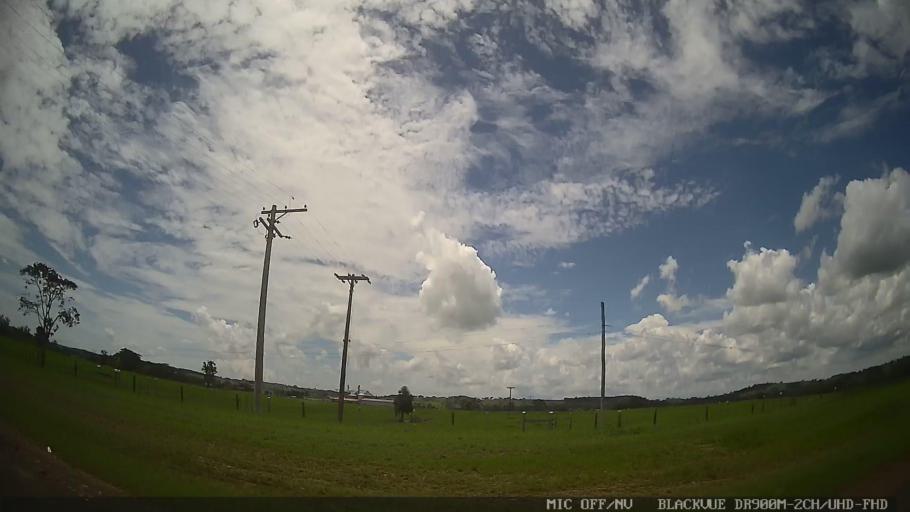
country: BR
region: Sao Paulo
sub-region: Conchas
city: Conchas
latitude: -23.0447
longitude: -47.9423
